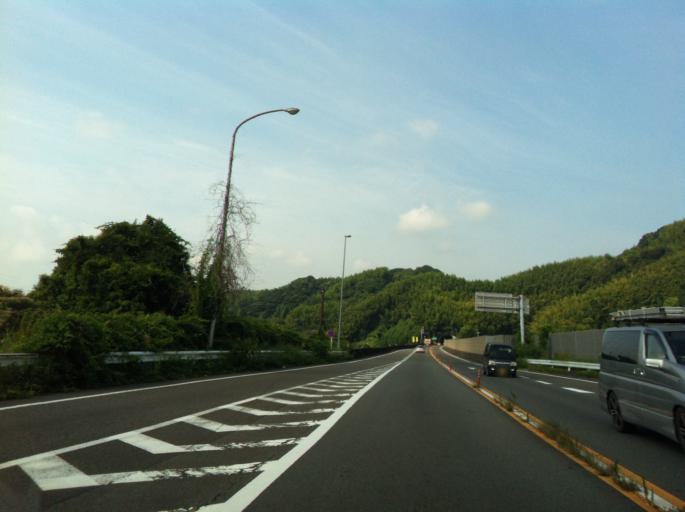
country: JP
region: Shizuoka
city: Fujieda
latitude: 34.8968
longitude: 138.2763
